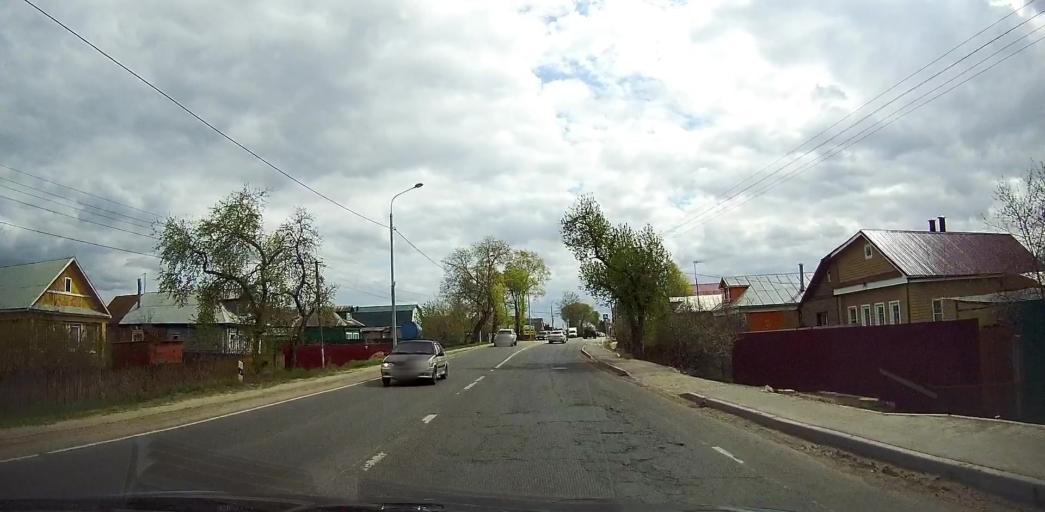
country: RU
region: Moskovskaya
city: Beloozerskiy
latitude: 55.4483
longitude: 38.4506
